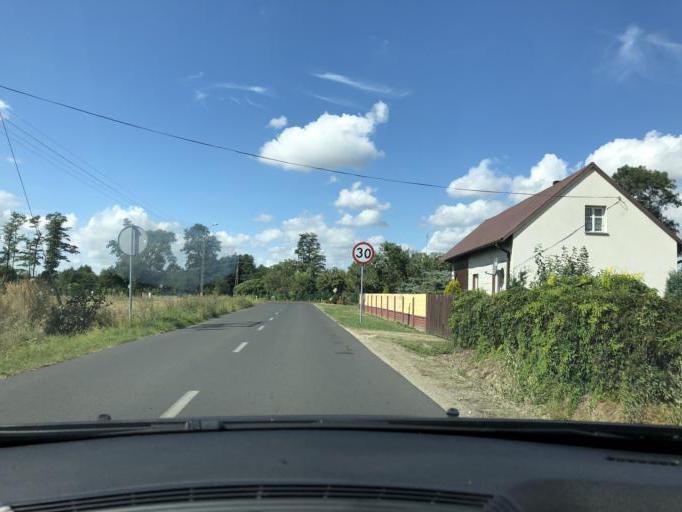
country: PL
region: Lodz Voivodeship
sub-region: Powiat wieruszowski
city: Walichnowy
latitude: 51.2456
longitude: 18.3729
